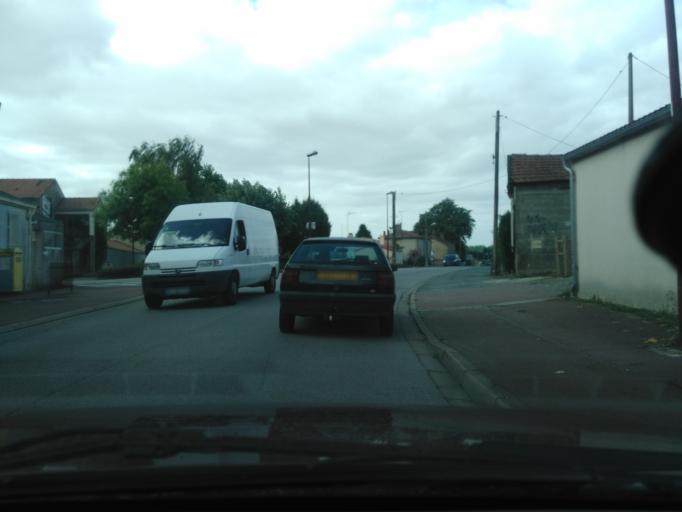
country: FR
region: Pays de la Loire
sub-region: Departement de la Vendee
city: La Ferriere
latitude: 46.7119
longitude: -1.3151
